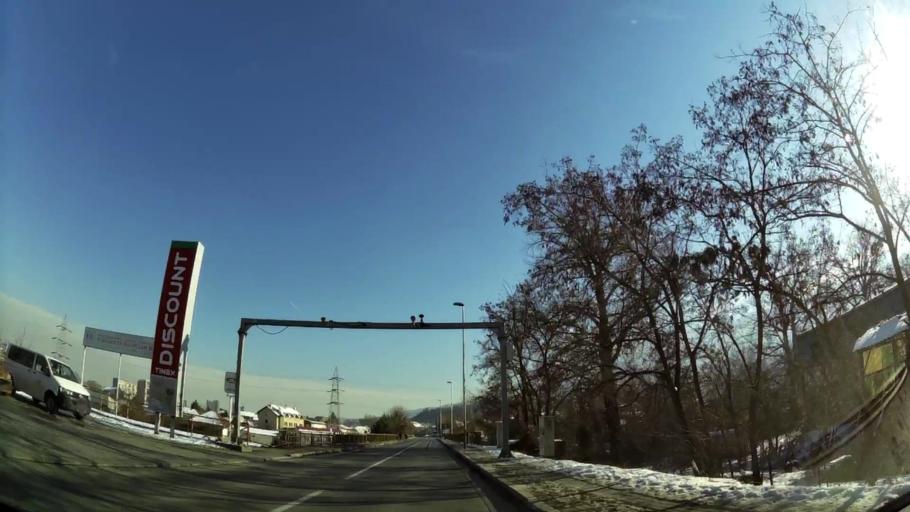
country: MK
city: Krushopek
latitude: 42.0018
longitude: 21.3766
